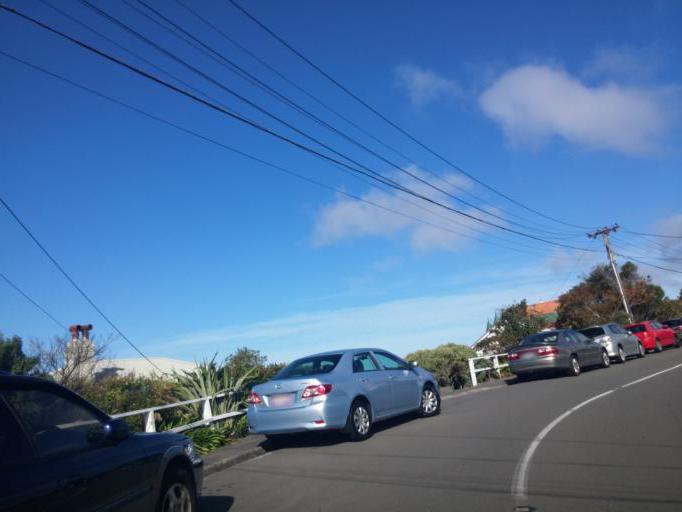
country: NZ
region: Wellington
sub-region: Wellington City
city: Kelburn
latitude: -41.2887
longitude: 174.7506
